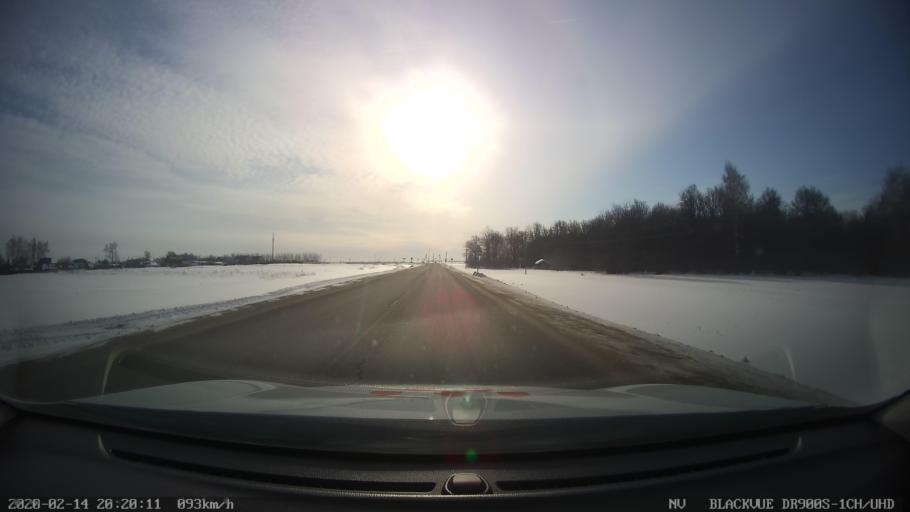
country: RU
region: Tatarstan
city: Verkhniy Uslon
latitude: 55.5597
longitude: 48.9024
